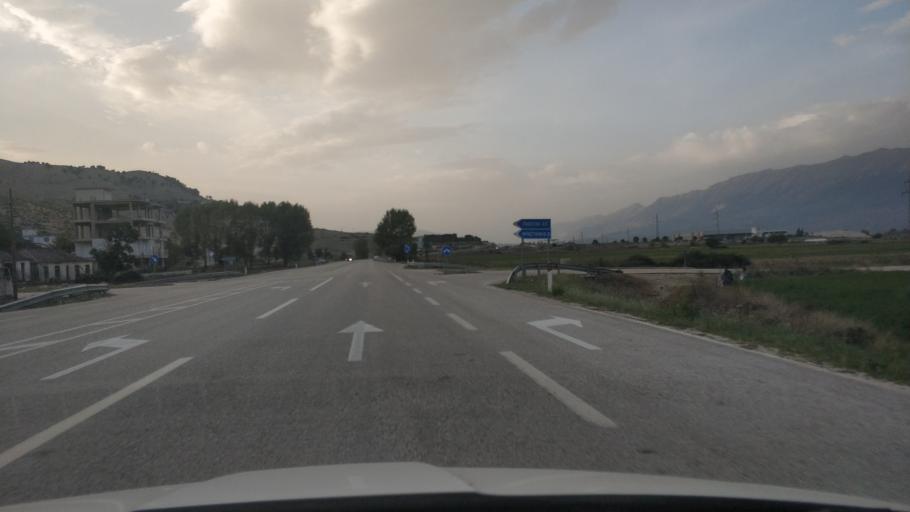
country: AL
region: Gjirokaster
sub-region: Rrethi i Gjirokastres
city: Libohove
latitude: 39.9670
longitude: 20.2397
